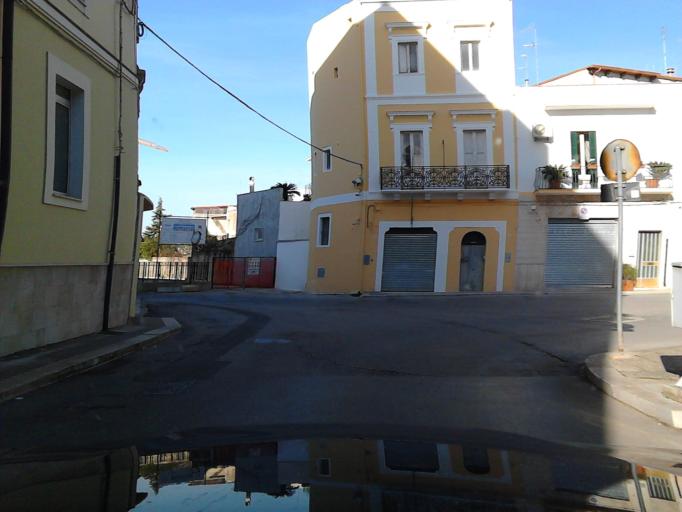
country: IT
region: Apulia
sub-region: Provincia di Bari
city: Rutigliano
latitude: 41.0119
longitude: 17.0023
